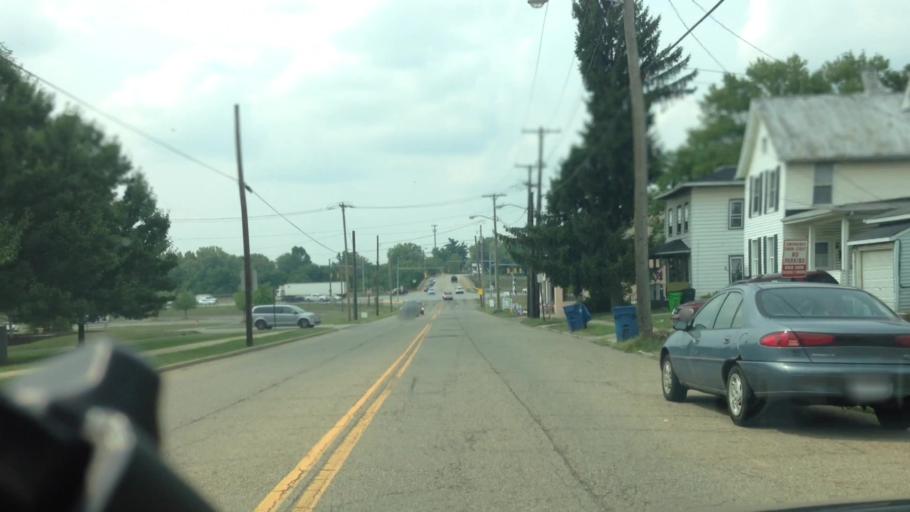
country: US
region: Ohio
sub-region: Stark County
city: Massillon
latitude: 40.8007
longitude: -81.5263
